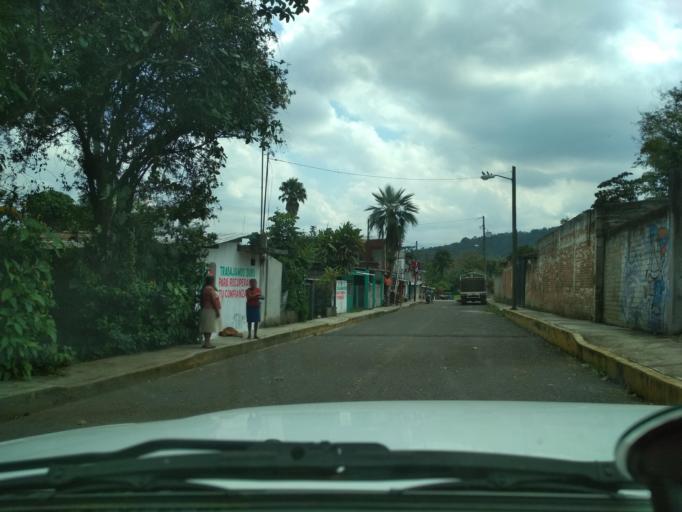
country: MX
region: Veracruz
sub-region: Fortin
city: Monte Salas
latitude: 18.9366
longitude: -97.0181
